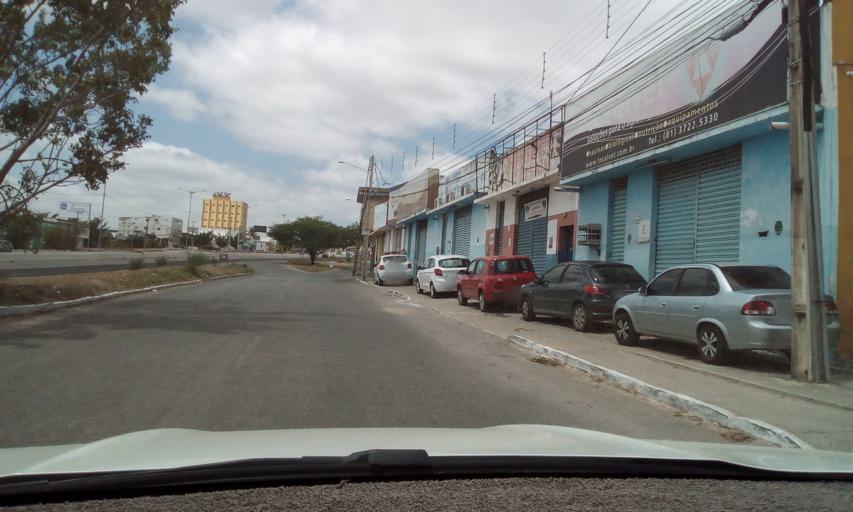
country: BR
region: Pernambuco
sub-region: Caruaru
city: Caruaru
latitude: -8.2920
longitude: -35.9858
